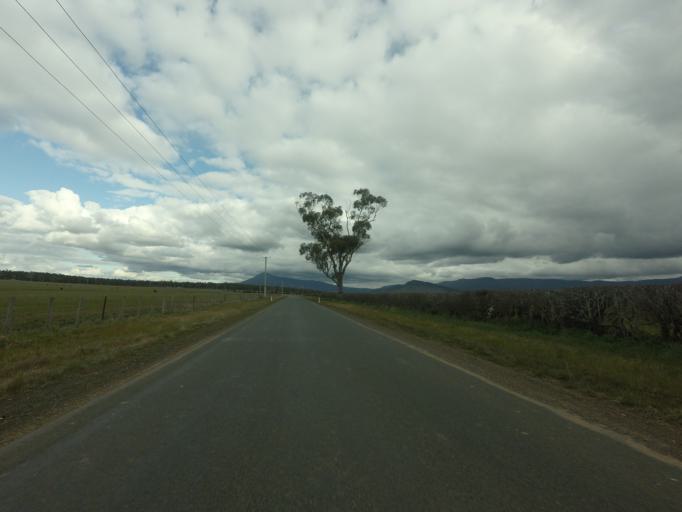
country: AU
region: Tasmania
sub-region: Northern Midlands
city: Longford
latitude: -41.7916
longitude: 147.1132
